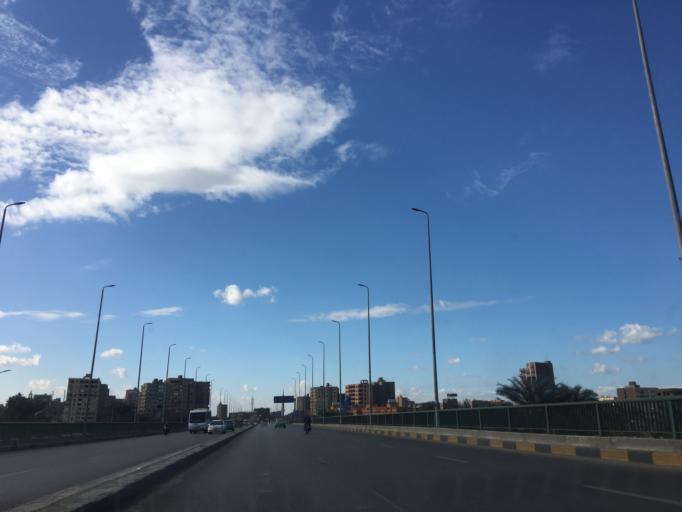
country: EG
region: Al Jizah
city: Al Jizah
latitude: 30.0290
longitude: 31.1914
